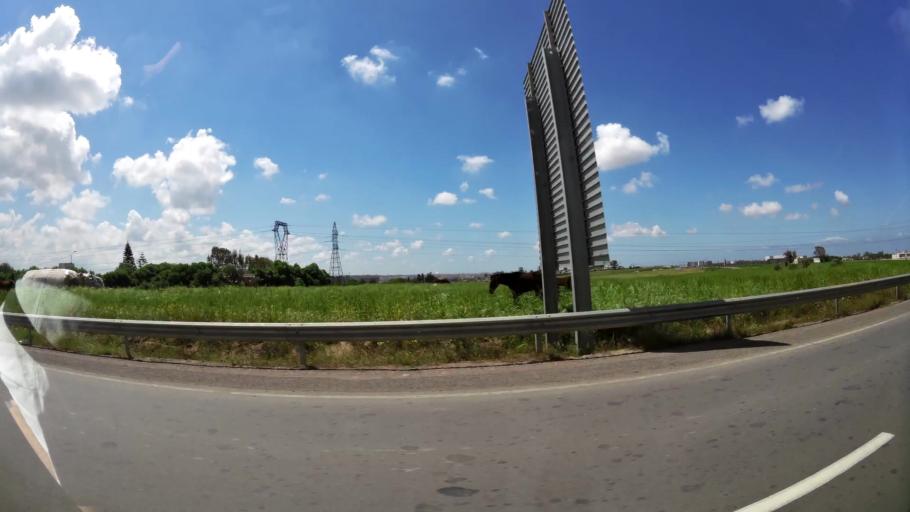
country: MA
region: Grand Casablanca
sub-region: Casablanca
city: Casablanca
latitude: 33.5190
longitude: -7.6156
